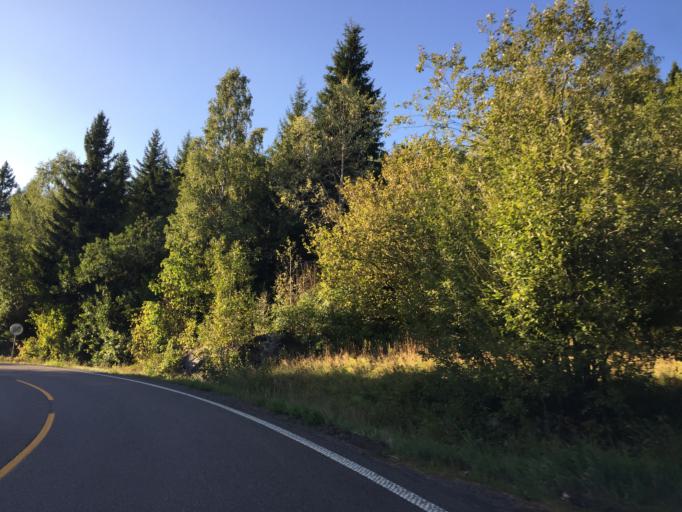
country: NO
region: Akershus
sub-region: Enebakk
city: Flateby
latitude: 59.8053
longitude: 11.2578
